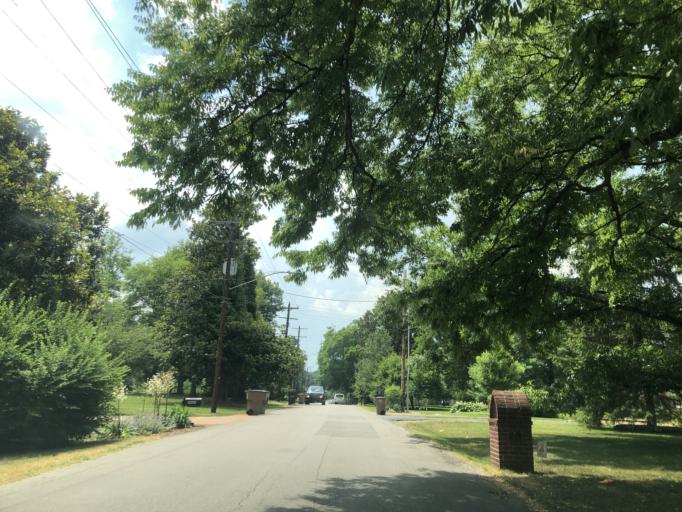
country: US
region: Tennessee
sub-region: Davidson County
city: Belle Meade
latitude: 36.1173
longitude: -86.8233
